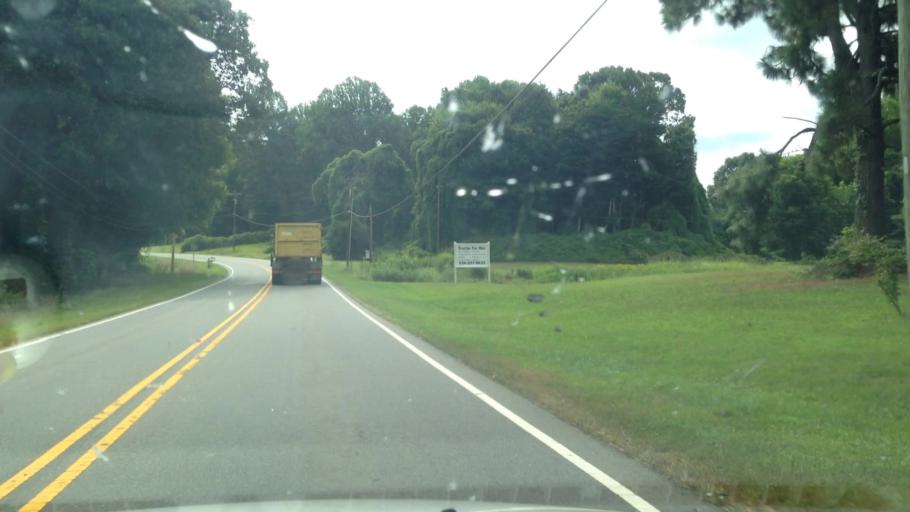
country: US
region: North Carolina
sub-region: Rockingham County
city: Wentworth
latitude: 36.3974
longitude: -79.7663
